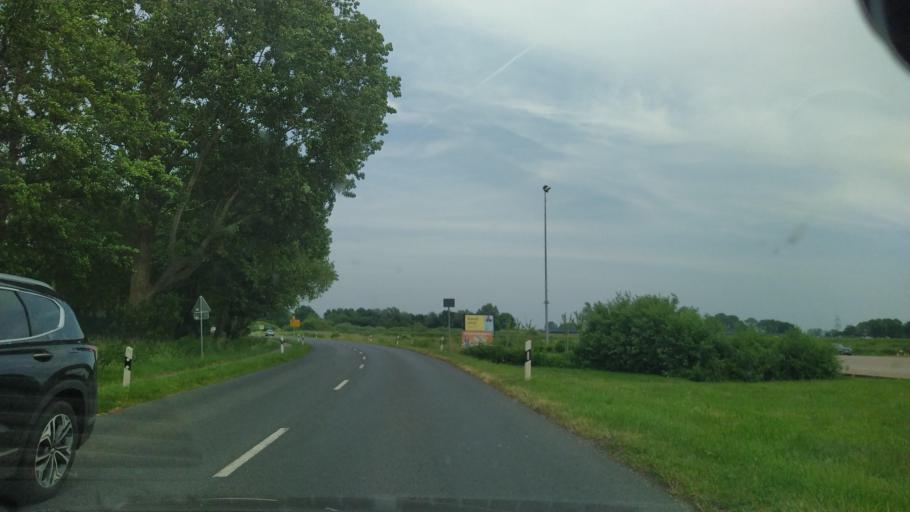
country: DE
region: Lower Saxony
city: Leer
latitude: 53.2214
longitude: 7.4771
